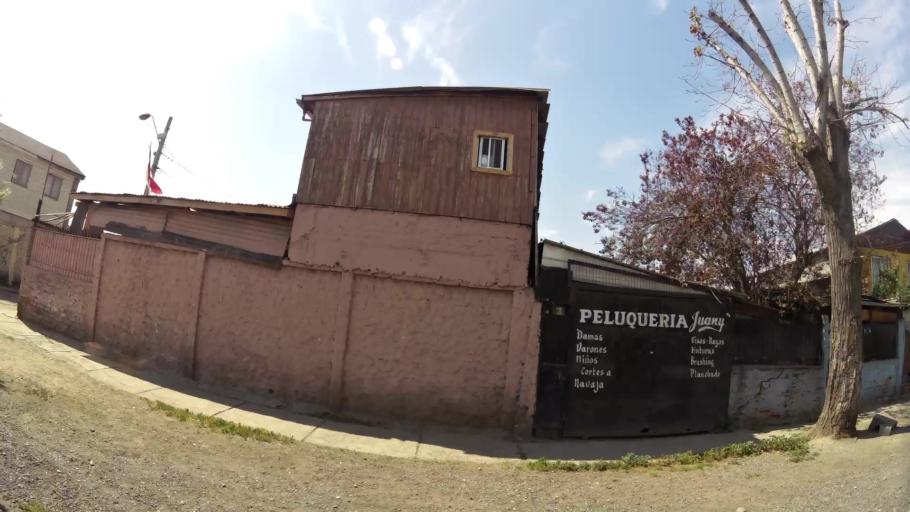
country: CL
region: Santiago Metropolitan
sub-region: Provincia de Santiago
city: La Pintana
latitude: -33.5503
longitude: -70.6366
